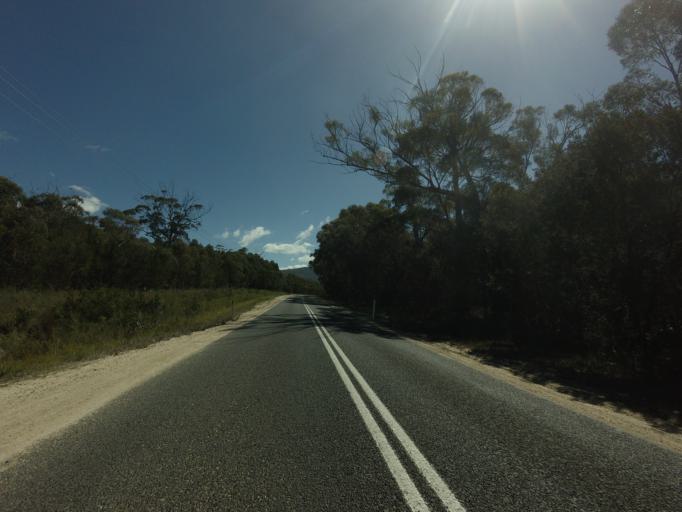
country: AU
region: Tasmania
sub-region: Break O'Day
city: St Helens
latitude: -41.8476
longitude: 148.2573
